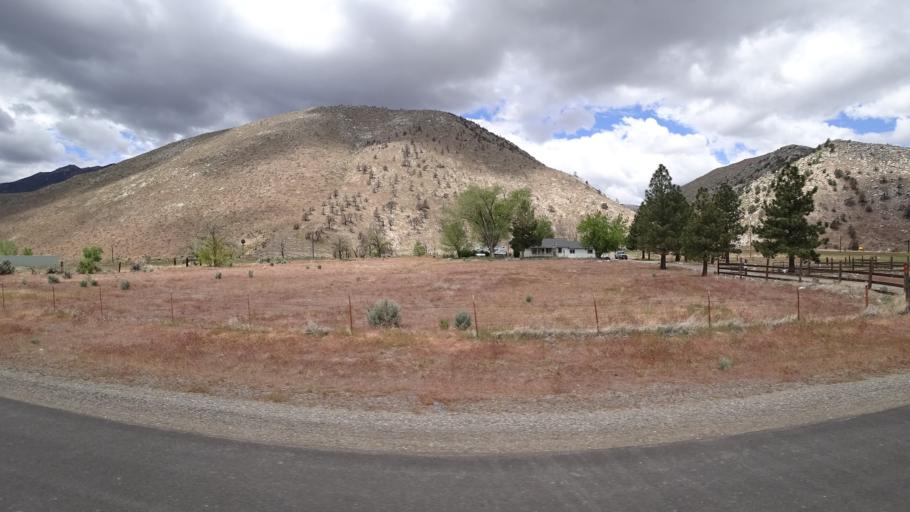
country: US
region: Nevada
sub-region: Lyon County
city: Smith Valley
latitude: 38.6408
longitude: -119.5269
